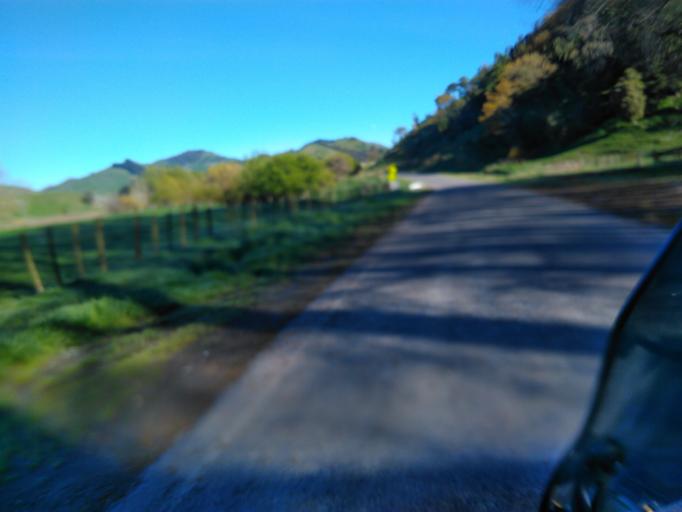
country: NZ
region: Gisborne
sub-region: Gisborne District
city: Gisborne
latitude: -38.4543
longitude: 177.7720
